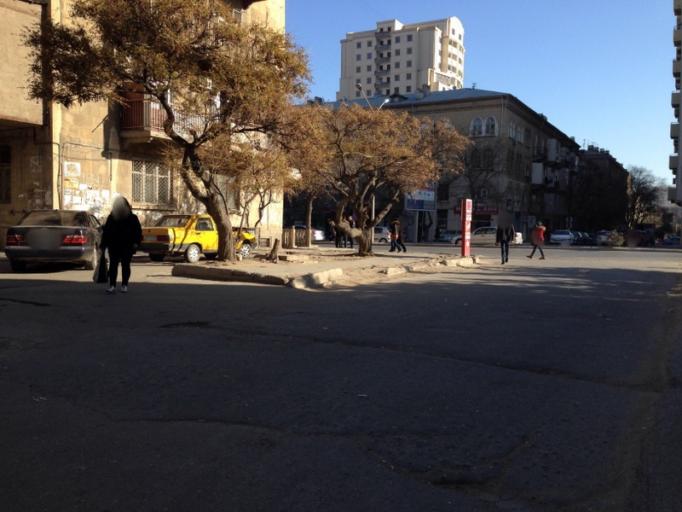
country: AZ
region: Baki
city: Baku
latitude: 40.4011
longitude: 49.8675
